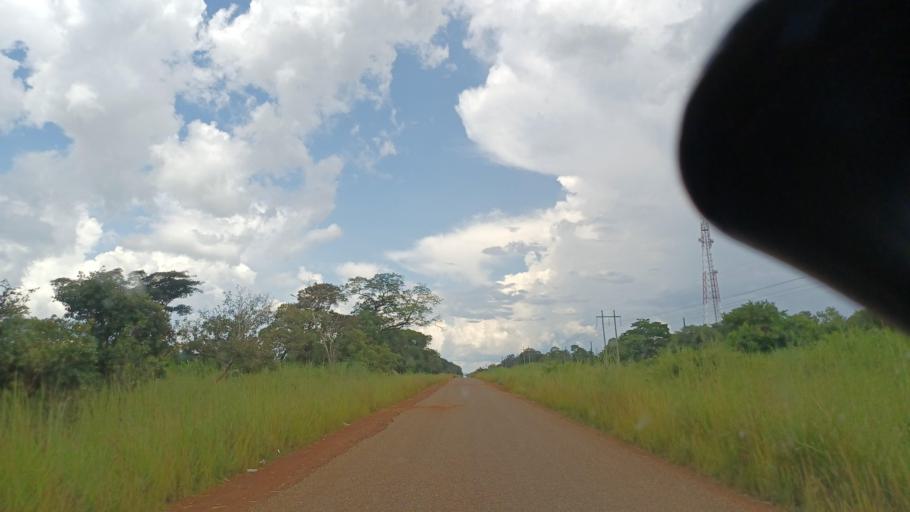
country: ZM
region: North-Western
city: Kasempa
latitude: -12.7945
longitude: 26.0158
